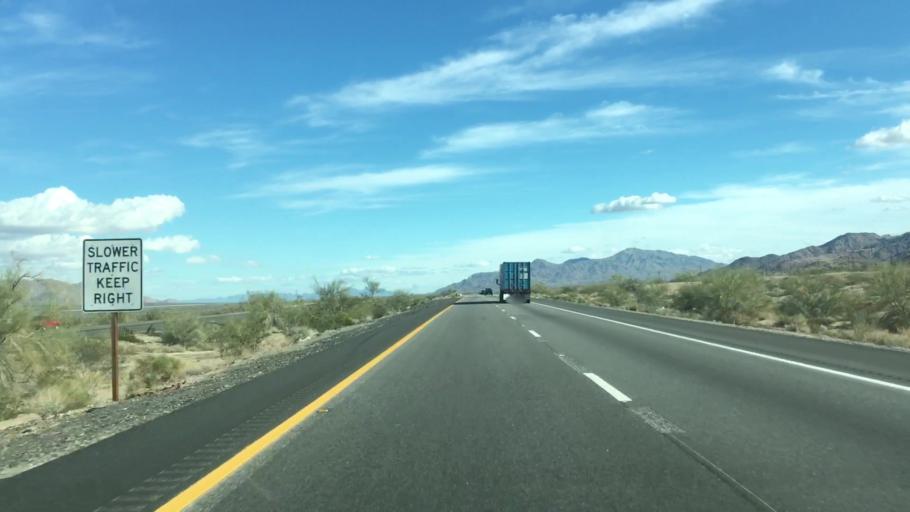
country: US
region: California
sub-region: Imperial County
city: Niland
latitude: 33.6690
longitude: -115.6418
